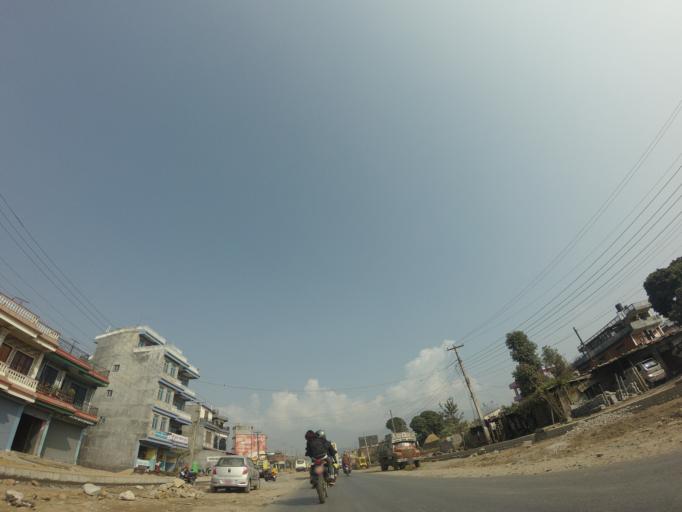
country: NP
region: Western Region
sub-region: Gandaki Zone
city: Pokhara
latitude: 28.2297
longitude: 83.9817
